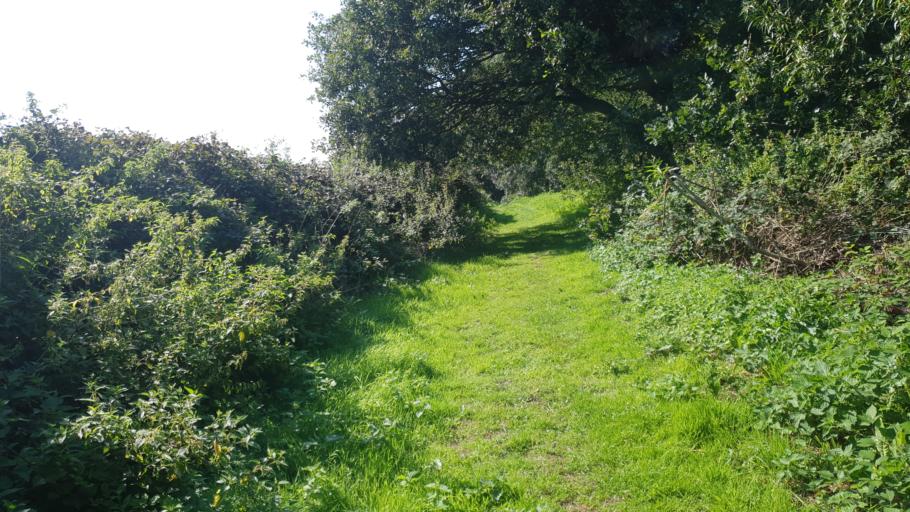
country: GB
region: England
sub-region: Essex
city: Wivenhoe
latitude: 51.9244
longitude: 0.9669
